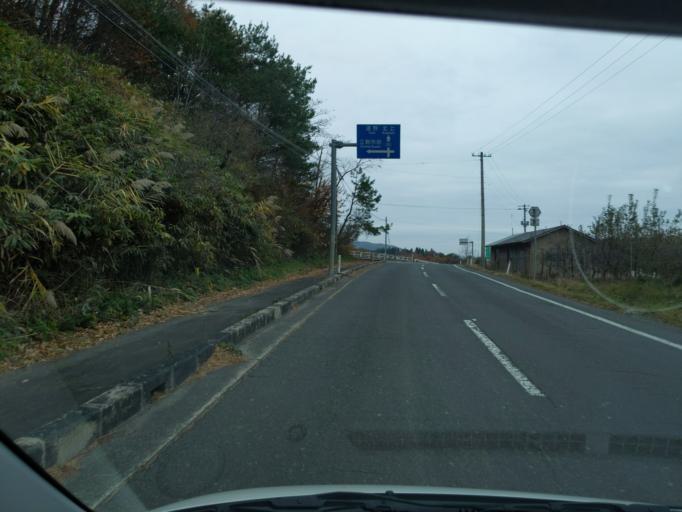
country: JP
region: Iwate
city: Mizusawa
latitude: 39.2029
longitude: 141.2195
